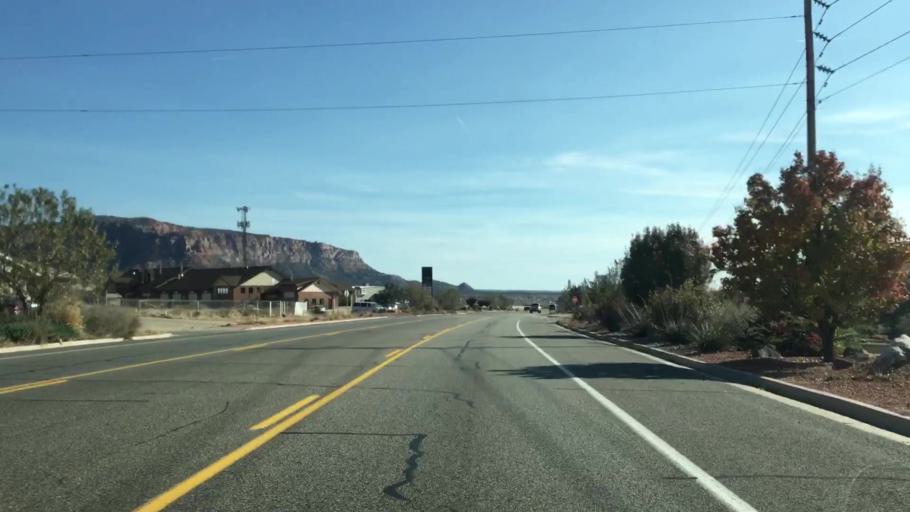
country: US
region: Arizona
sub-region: Mohave County
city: Colorado City
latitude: 37.0026
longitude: -113.0011
